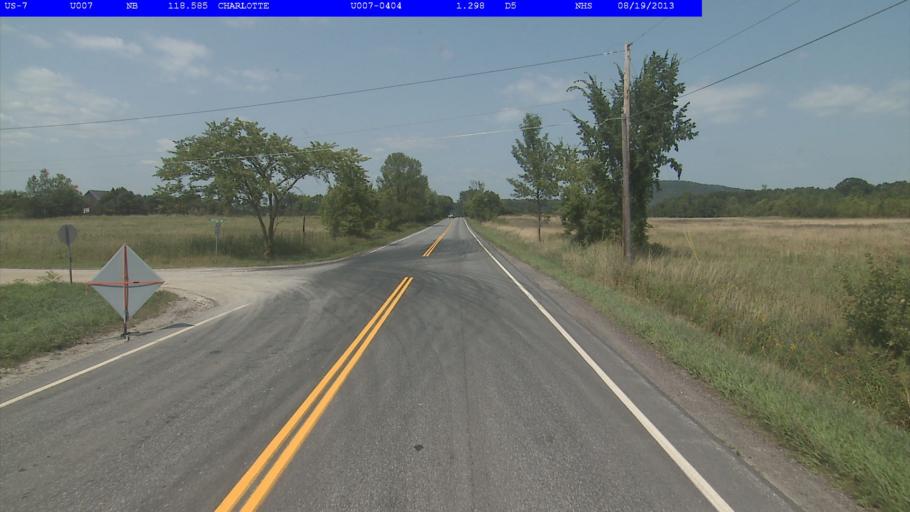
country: US
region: Vermont
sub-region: Addison County
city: Vergennes
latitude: 44.2808
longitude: -73.2360
